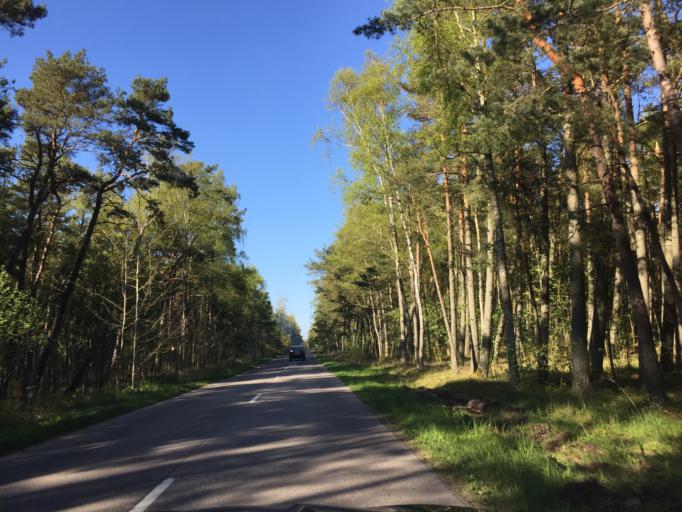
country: LT
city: Nida
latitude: 55.2053
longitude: 20.8741
